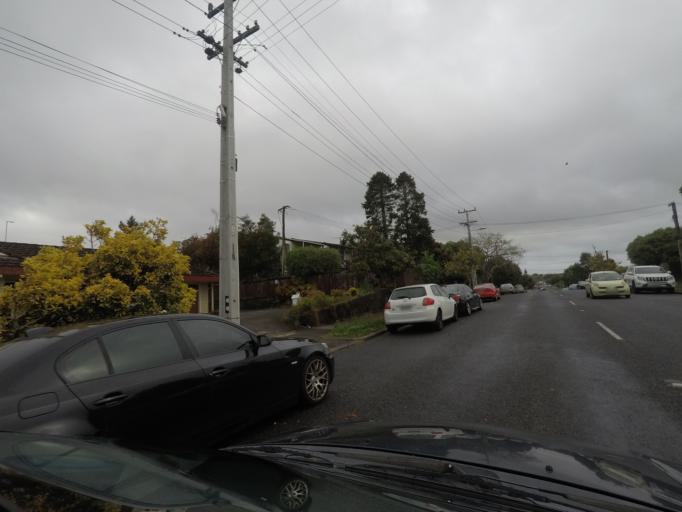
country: NZ
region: Auckland
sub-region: Auckland
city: Auckland
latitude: -36.8853
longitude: 174.7334
